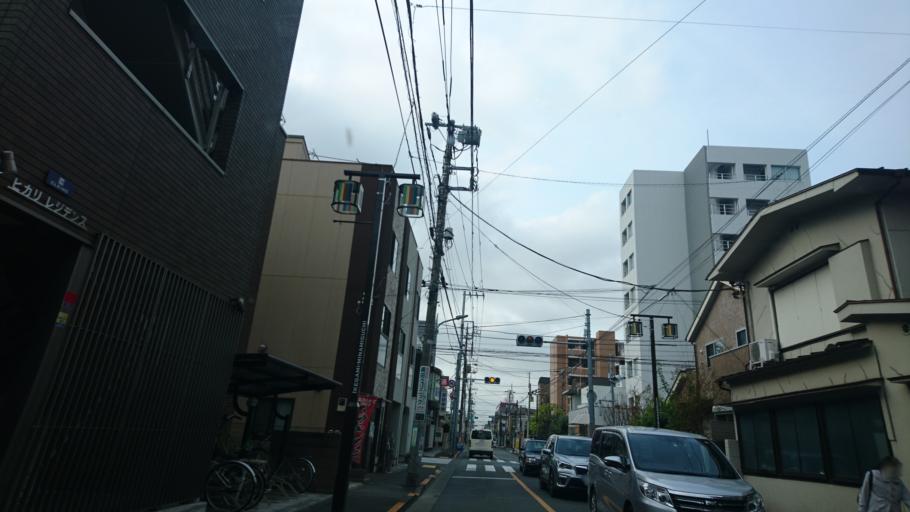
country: JP
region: Kanagawa
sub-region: Kawasaki-shi
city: Kawasaki
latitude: 35.5707
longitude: 139.7038
